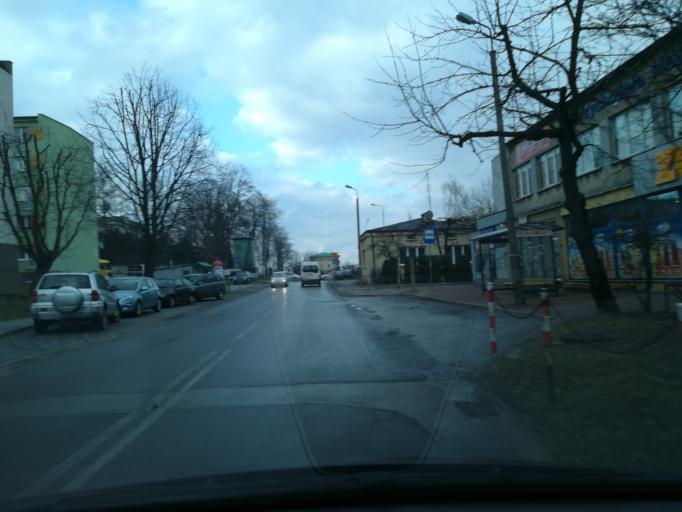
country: PL
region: Lodz Voivodeship
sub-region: Powiat radomszczanski
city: Radomsko
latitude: 51.0692
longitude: 19.4314
